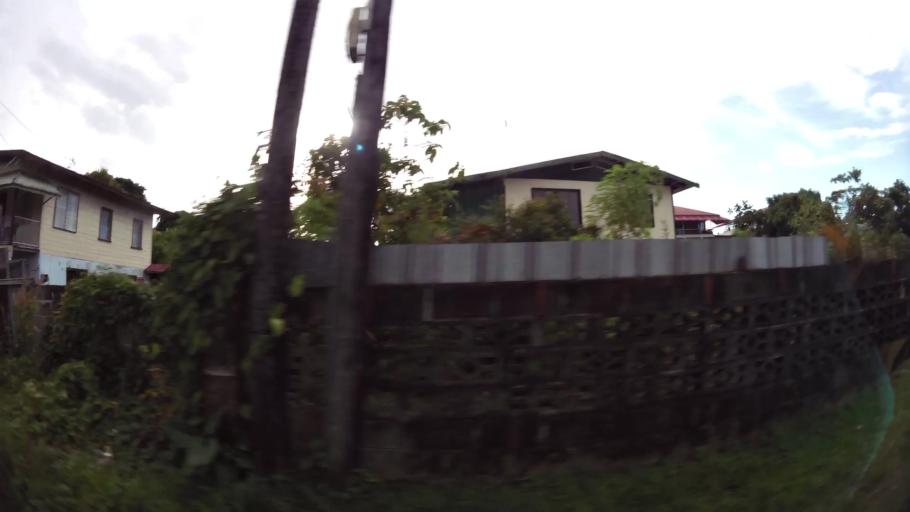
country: SR
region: Paramaribo
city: Paramaribo
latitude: 5.8374
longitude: -55.1789
